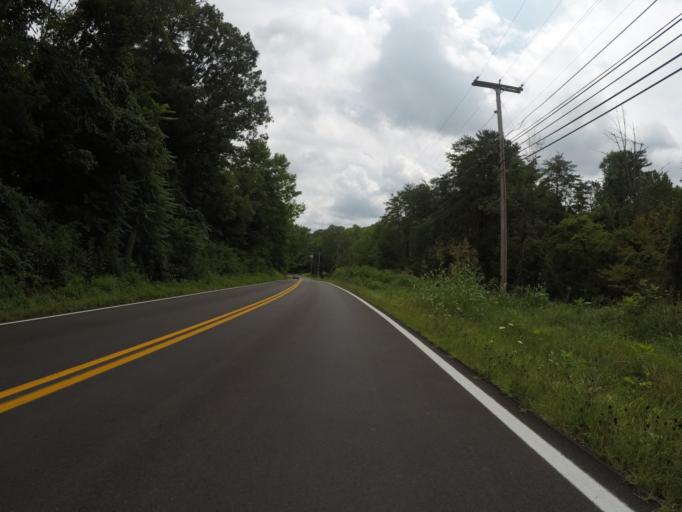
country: US
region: Kentucky
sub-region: Boyd County
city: Catlettsburg
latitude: 38.4208
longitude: -82.6088
